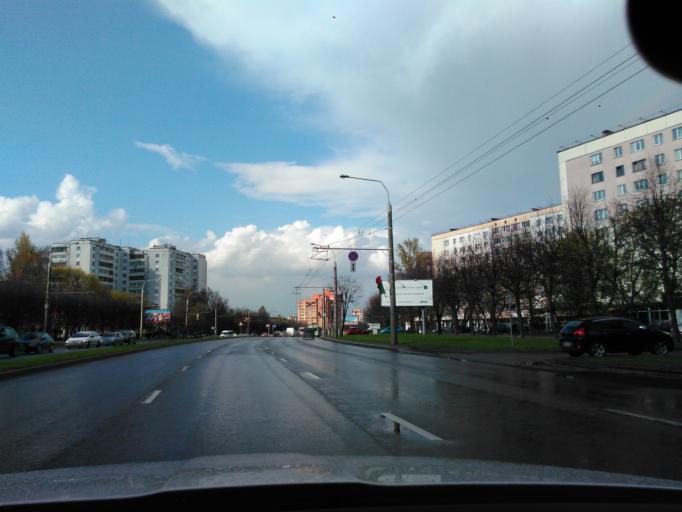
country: BY
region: Minsk
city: Novoye Medvezhino
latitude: 53.9165
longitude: 27.4952
